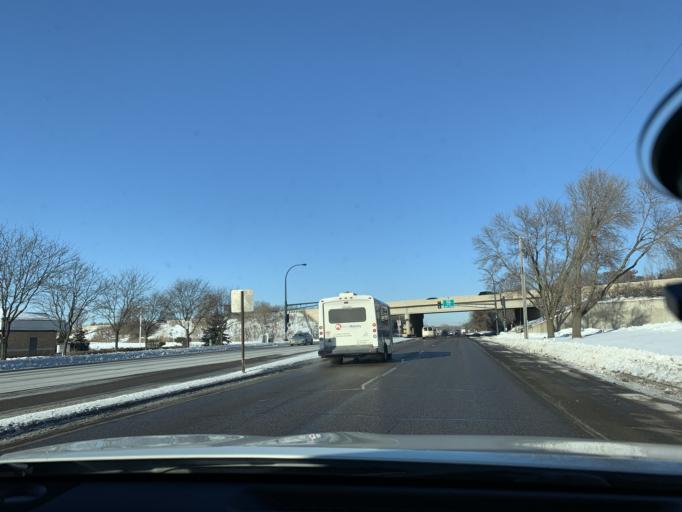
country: US
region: Minnesota
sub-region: Anoka County
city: Coon Rapids
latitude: 45.1418
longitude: -93.2779
